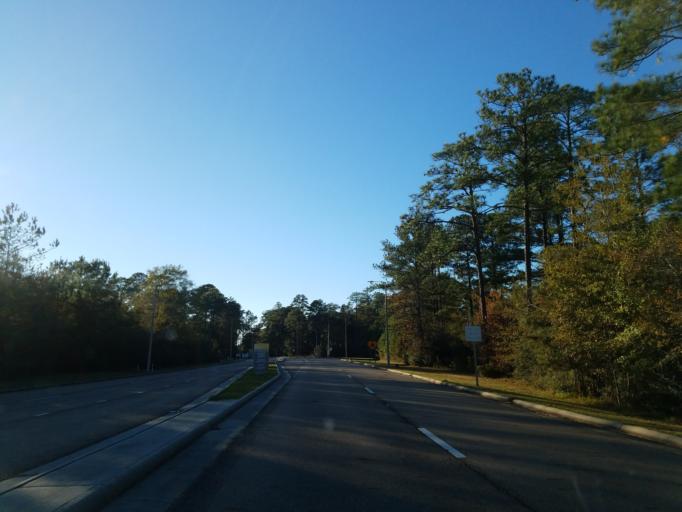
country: US
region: Mississippi
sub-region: Lamar County
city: Arnold Line
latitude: 31.3539
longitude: -89.3712
